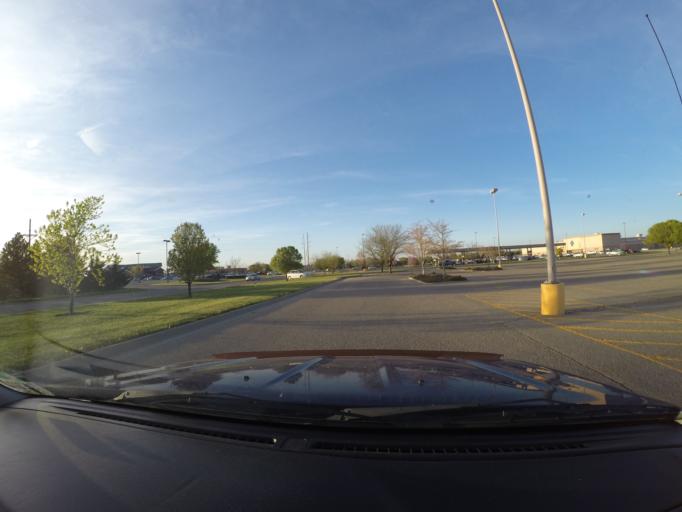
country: US
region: Kansas
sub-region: Saline County
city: Salina
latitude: 38.7842
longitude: -97.6109
